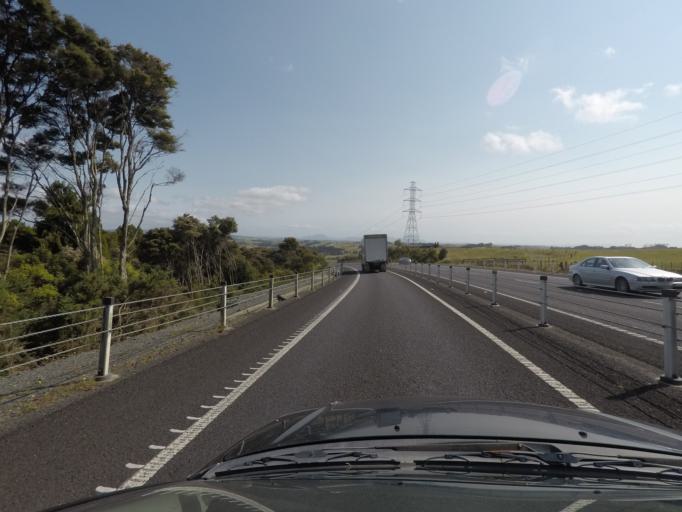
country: NZ
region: Northland
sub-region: Whangarei
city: Ruakaka
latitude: -36.0469
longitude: 174.4171
